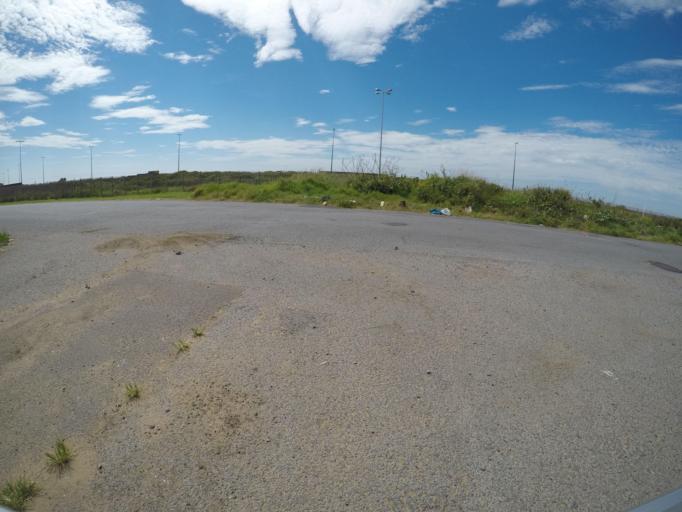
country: ZA
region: Eastern Cape
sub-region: Buffalo City Metropolitan Municipality
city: East London
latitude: -33.0336
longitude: 27.9098
